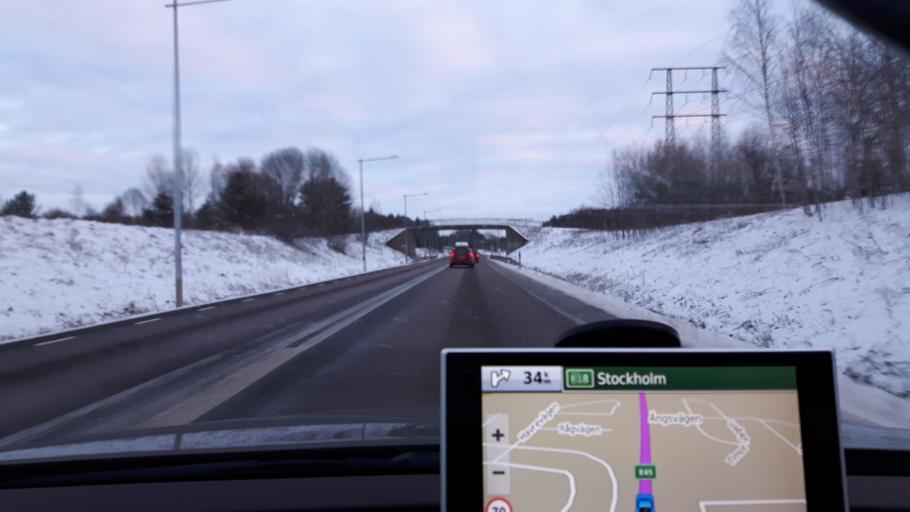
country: SE
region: Vaestra Goetaland
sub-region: Amals Kommun
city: Amal
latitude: 59.0600
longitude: 12.6785
